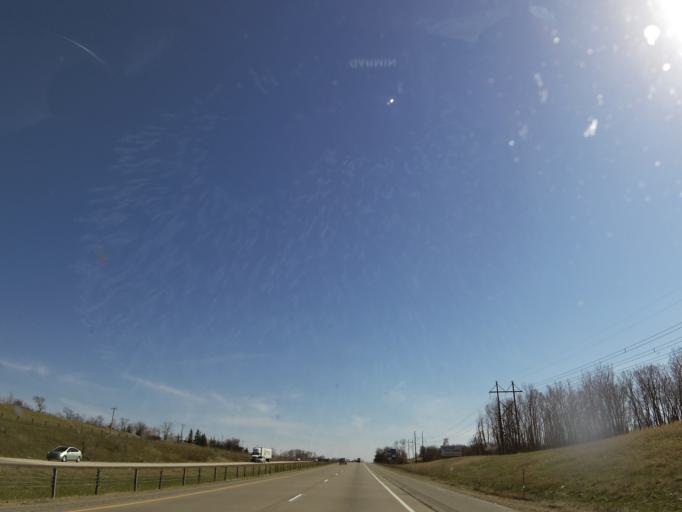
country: US
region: Minnesota
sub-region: Dakota County
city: Lakeville
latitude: 44.6664
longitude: -93.2942
